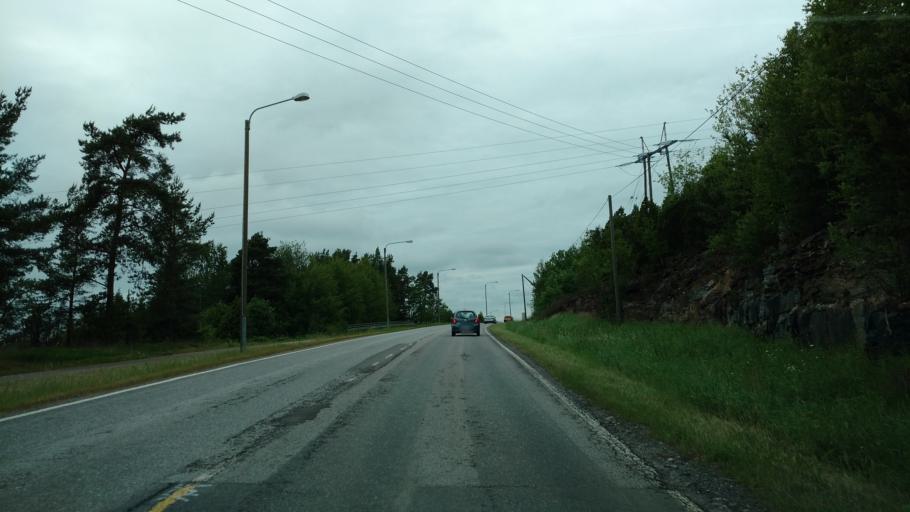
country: FI
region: Varsinais-Suomi
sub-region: Salo
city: Halikko
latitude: 60.4108
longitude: 23.0570
